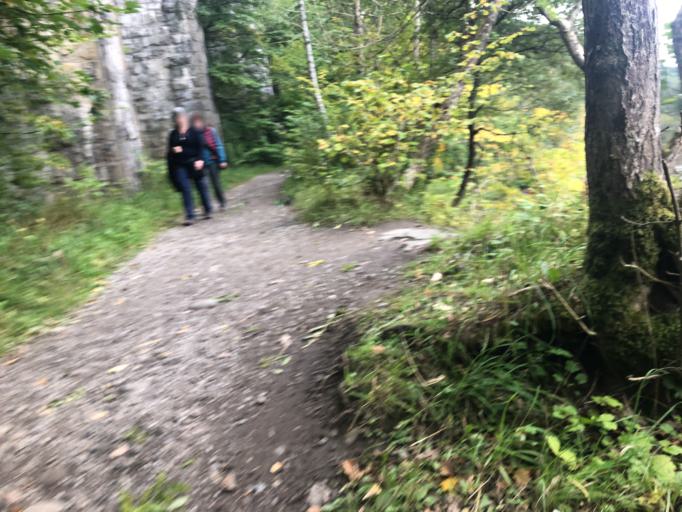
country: GB
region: Scotland
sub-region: Perth and Kinross
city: Pitlochry
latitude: 56.7419
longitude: -3.7728
